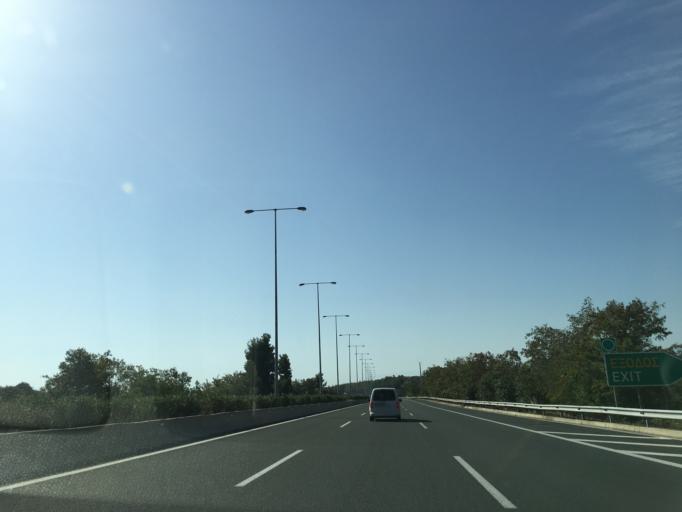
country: GR
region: Central Macedonia
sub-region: Nomos Pierias
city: Makrygialos
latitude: 40.4207
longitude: 22.5903
